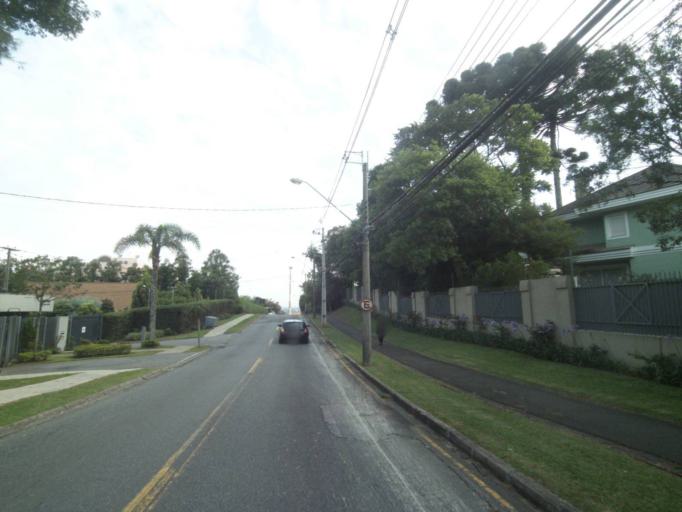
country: BR
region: Parana
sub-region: Curitiba
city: Curitiba
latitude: -25.4205
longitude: -49.3198
